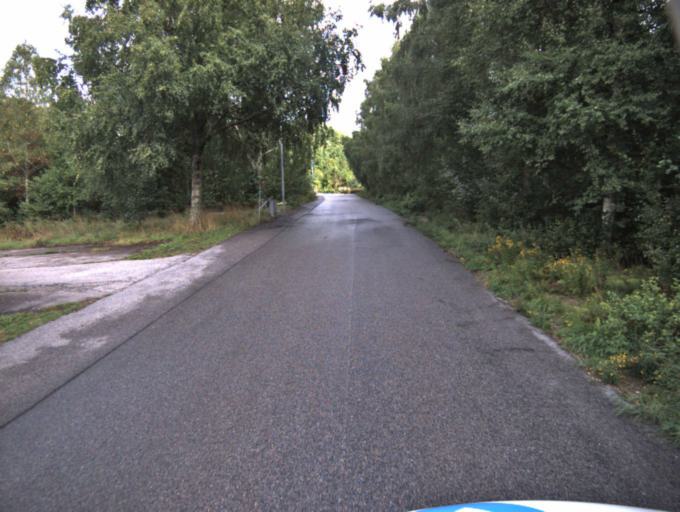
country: SE
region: Vaestra Goetaland
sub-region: Tranemo Kommun
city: Langhem
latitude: 57.6964
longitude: 13.3045
